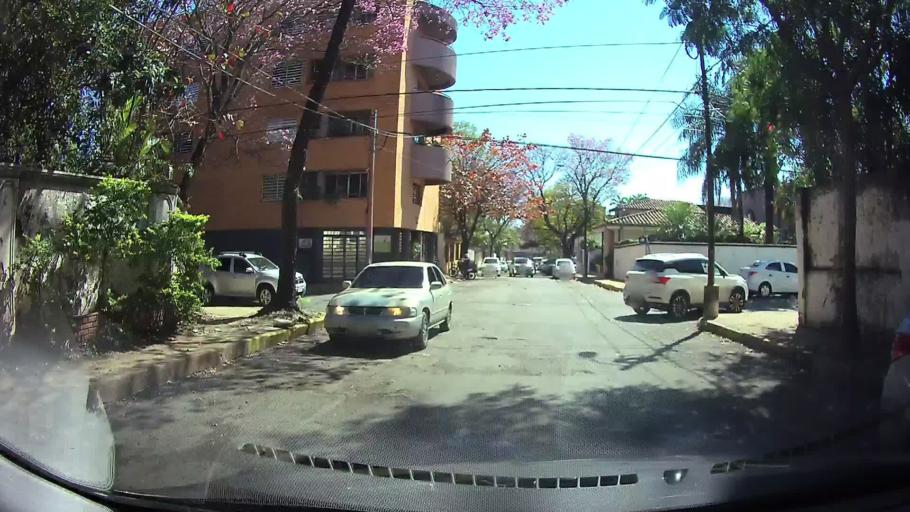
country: PY
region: Asuncion
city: Asuncion
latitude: -25.2831
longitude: -57.6179
